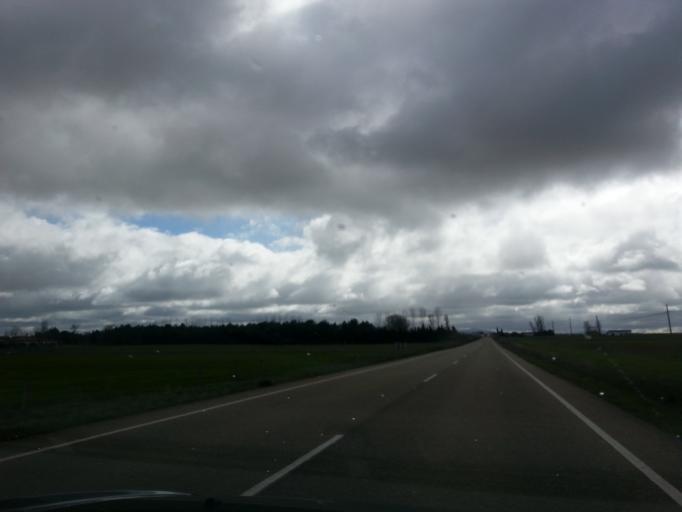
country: ES
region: Castille and Leon
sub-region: Provincia de Salamanca
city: La Fuente de San Esteban
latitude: 40.7818
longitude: -6.2344
